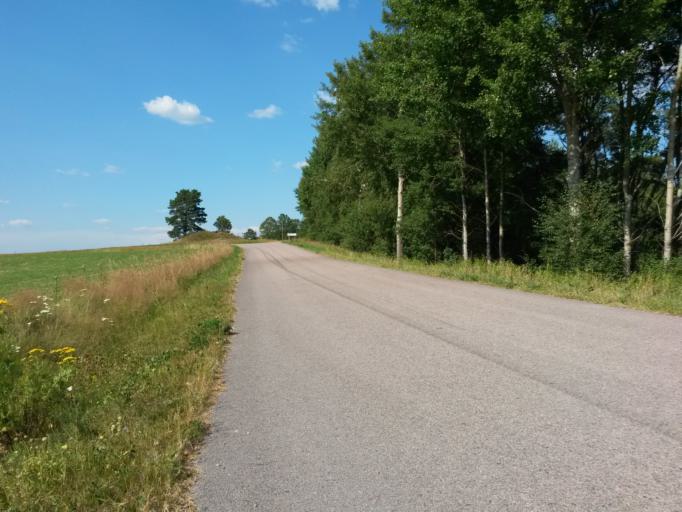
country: SE
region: Vaestra Goetaland
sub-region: Vargarda Kommun
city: Jonstorp
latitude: 57.9798
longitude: 12.6601
